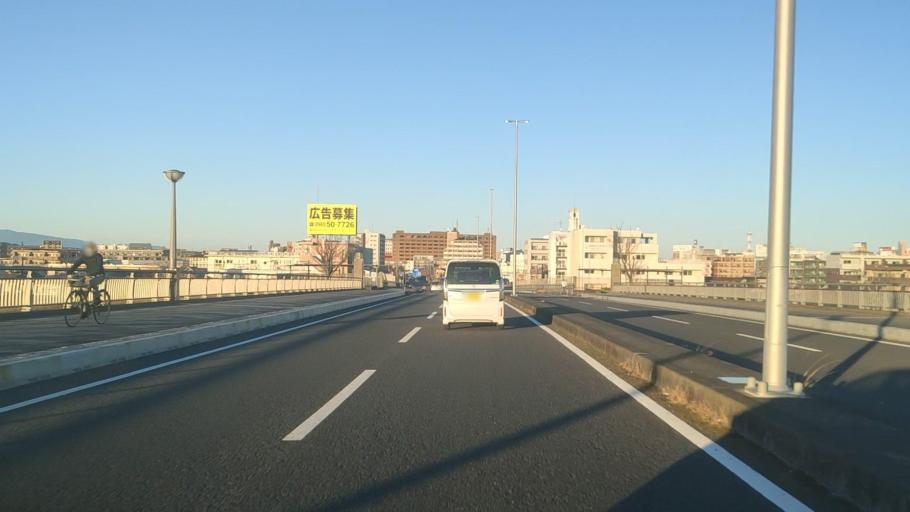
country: JP
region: Miyazaki
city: Miyazaki-shi
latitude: 31.9094
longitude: 131.4122
